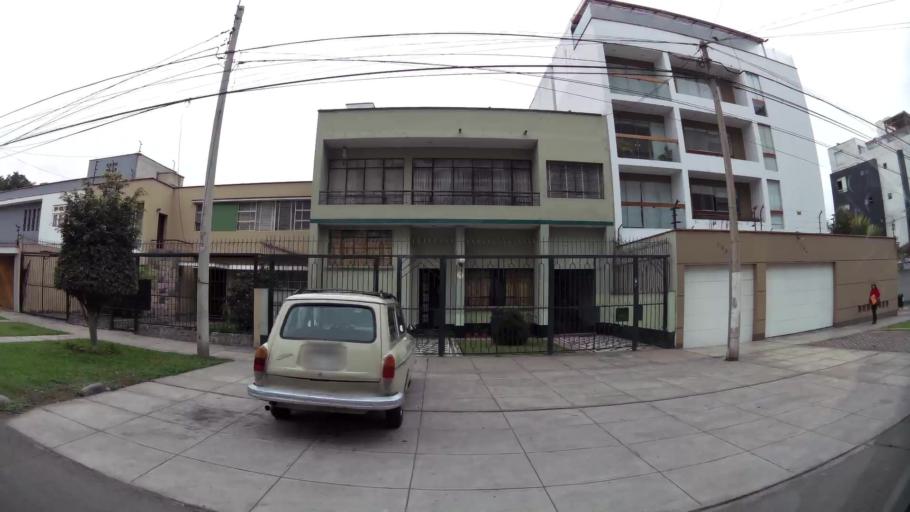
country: PE
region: Lima
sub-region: Lima
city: Surco
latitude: -12.1194
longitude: -77.0165
